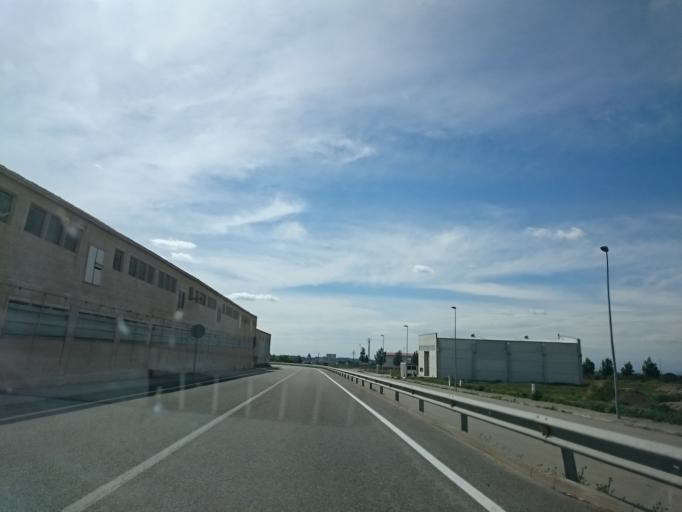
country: ES
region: Catalonia
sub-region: Provincia de Lleida
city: Sant Guim de Freixenet
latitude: 41.6433
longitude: 1.4189
